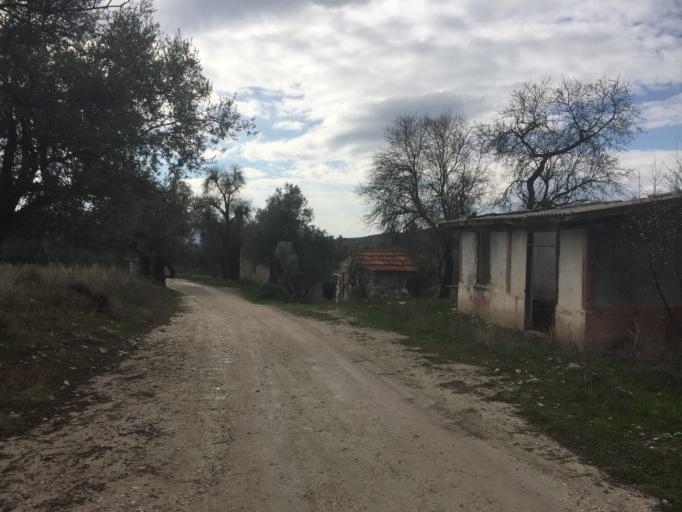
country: CY
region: Limassol
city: Pachna
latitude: 34.8912
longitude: 32.6585
